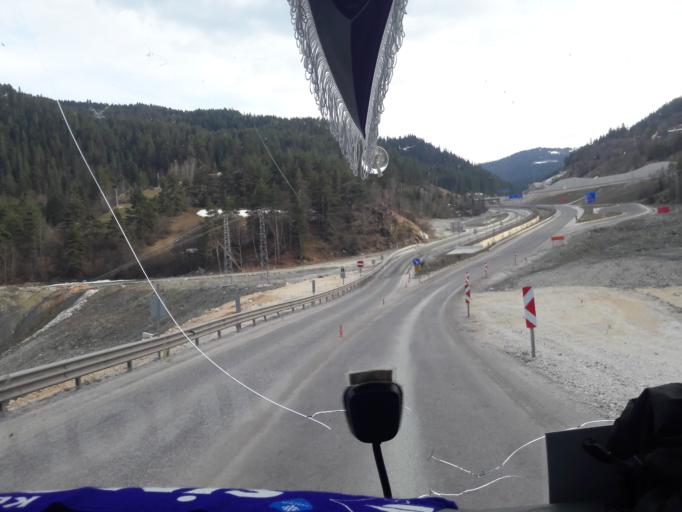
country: TR
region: Kastamonu
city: Kuzyaka
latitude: 41.1060
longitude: 33.7521
